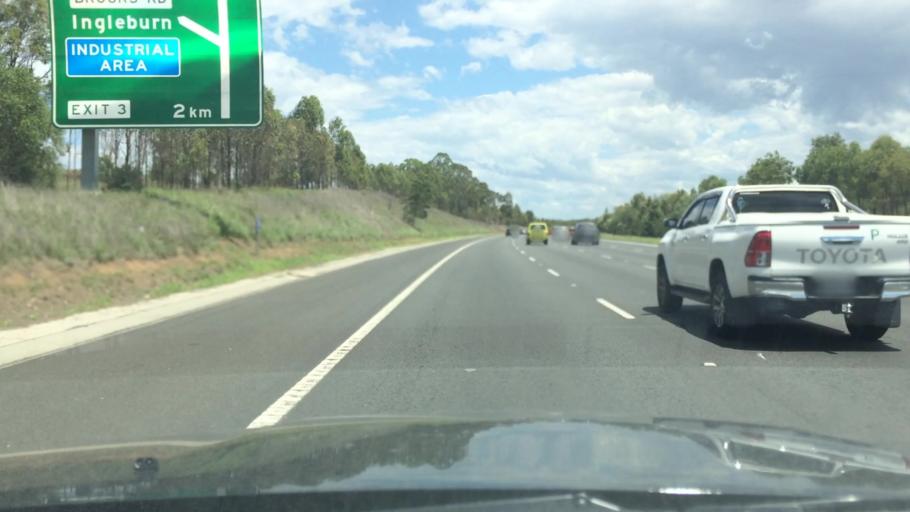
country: AU
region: New South Wales
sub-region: Campbelltown Municipality
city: Ingleburn
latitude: -33.9741
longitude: 150.8728
